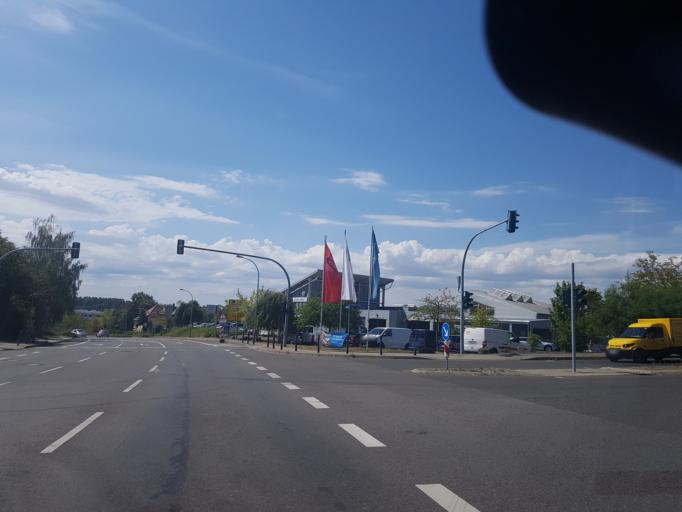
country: DE
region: Saxony
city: Waldheim
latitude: 51.0821
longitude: 12.9968
